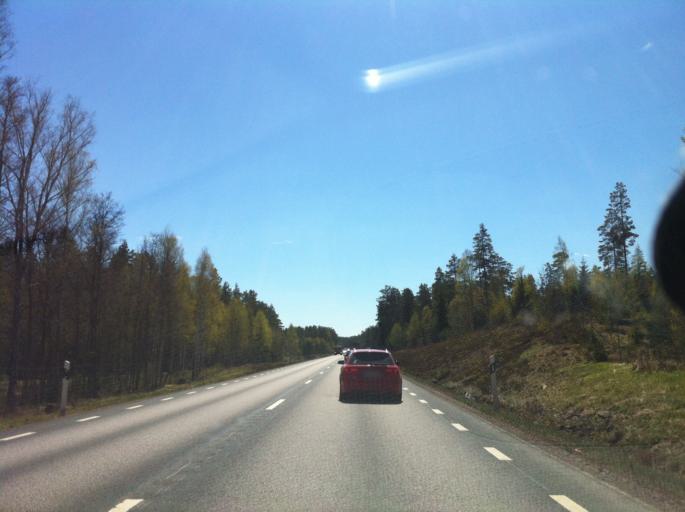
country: SE
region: Kalmar
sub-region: Vimmerby Kommun
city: Vimmerby
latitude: 57.6501
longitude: 15.8389
